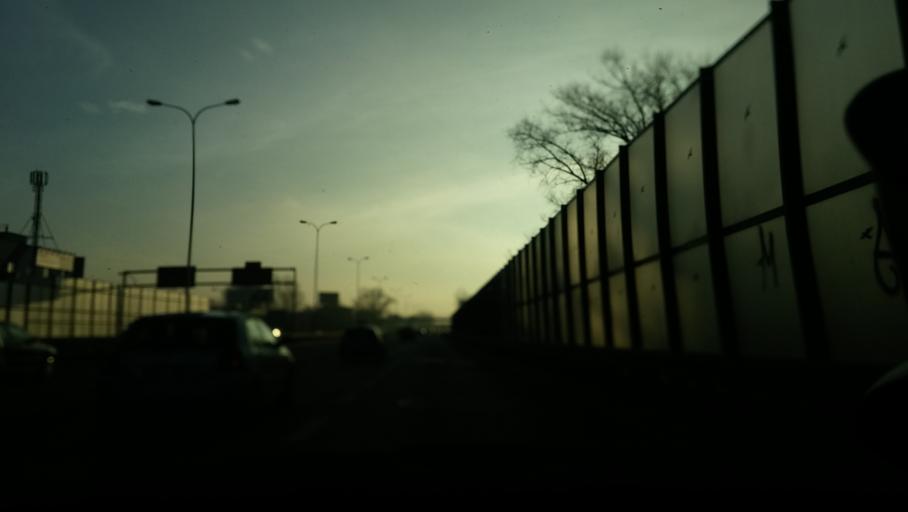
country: PL
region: Masovian Voivodeship
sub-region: Warszawa
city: Rembertow
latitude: 52.2314
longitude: 21.1330
